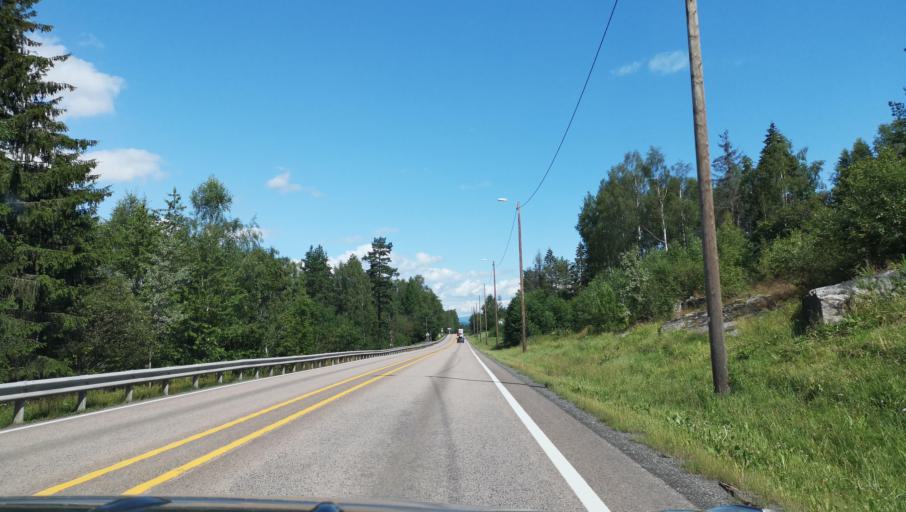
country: NO
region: Buskerud
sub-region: Ovre Eiker
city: Hokksund
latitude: 59.8624
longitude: 9.9115
